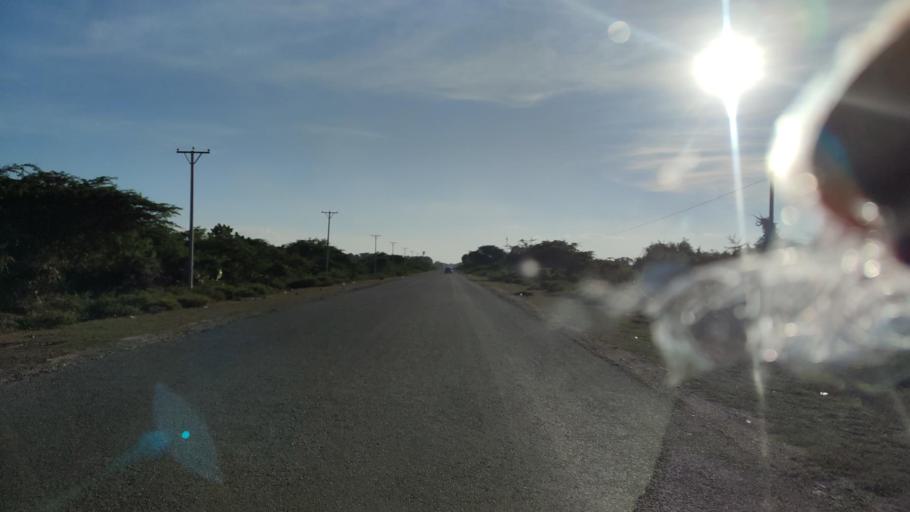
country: MM
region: Mandalay
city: Yamethin
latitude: 20.6189
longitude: 96.0783
